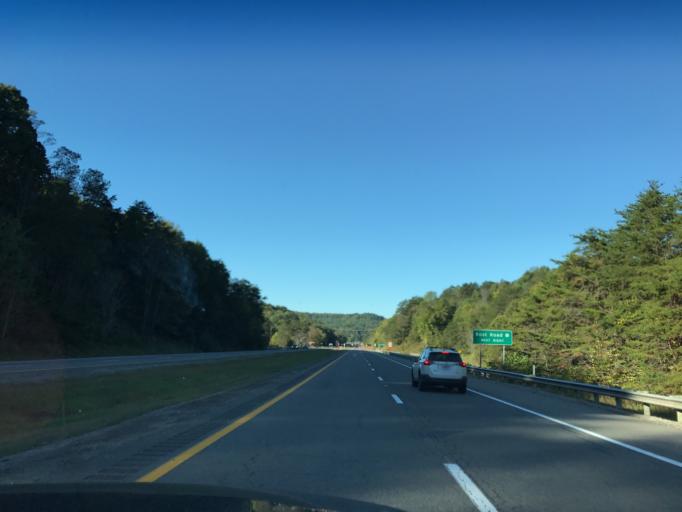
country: US
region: Ohio
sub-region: Washington County
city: Reno
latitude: 39.2524
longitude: -81.3468
